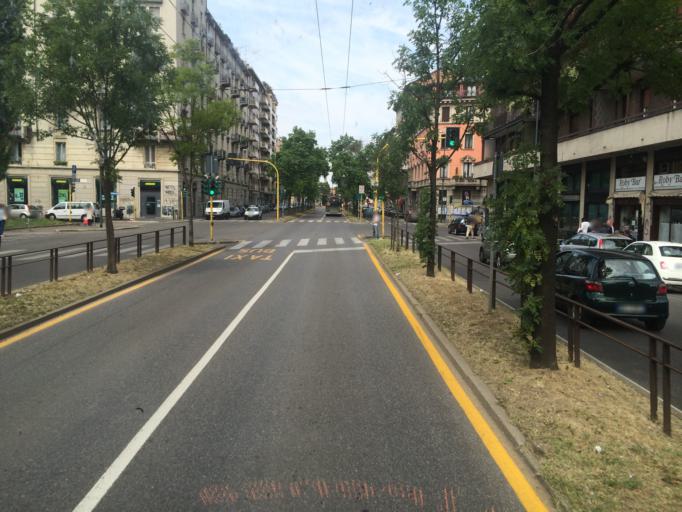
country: IT
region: Lombardy
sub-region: Citta metropolitana di Milano
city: Milano
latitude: 45.4938
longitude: 9.1882
